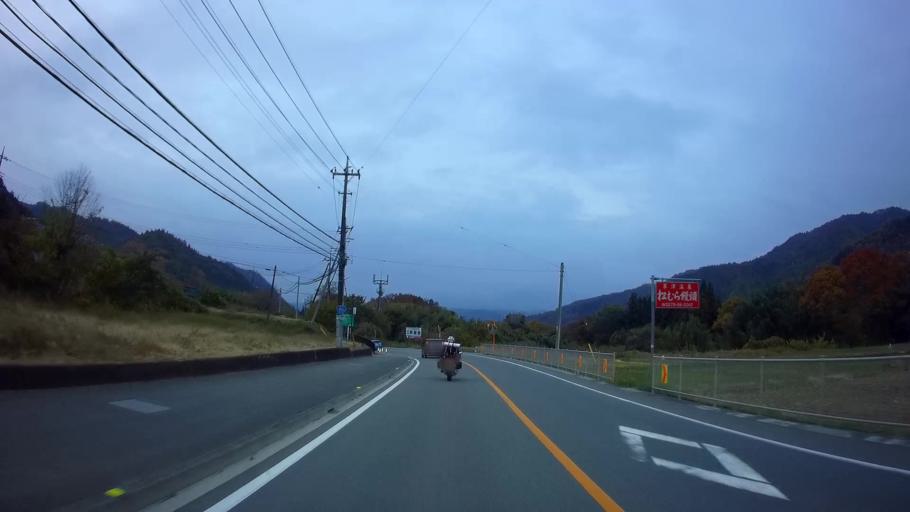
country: JP
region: Gunma
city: Nakanojomachi
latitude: 36.5609
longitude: 138.7626
